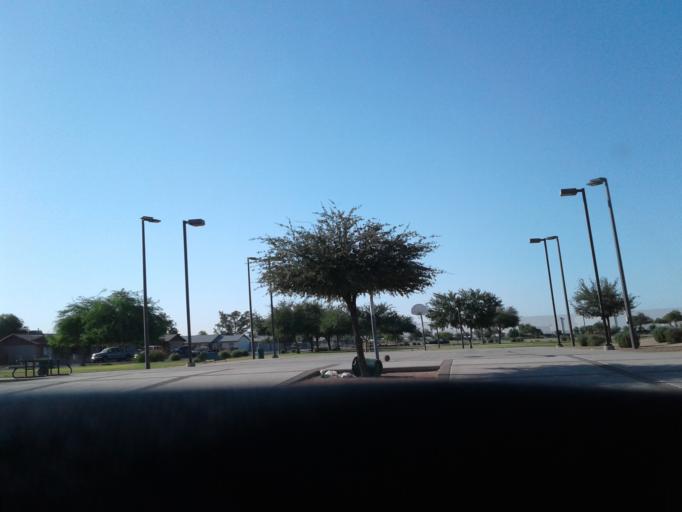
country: US
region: Arizona
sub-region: Maricopa County
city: Tolleson
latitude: 33.4577
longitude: -112.1942
